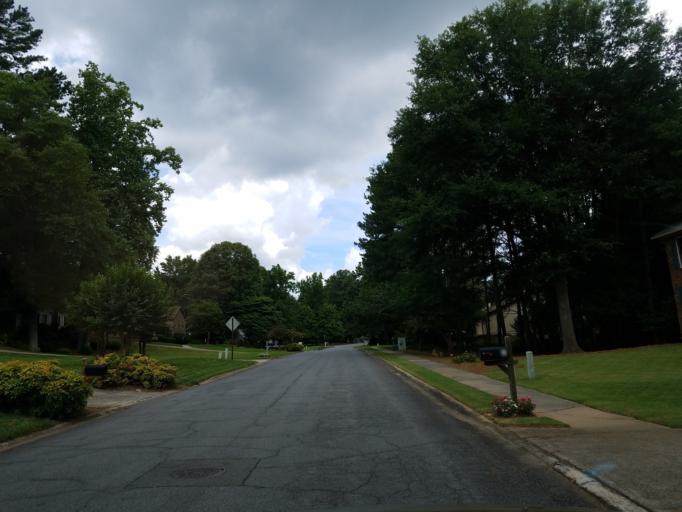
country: US
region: Georgia
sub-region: Cobb County
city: Marietta
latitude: 33.9546
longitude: -84.4804
